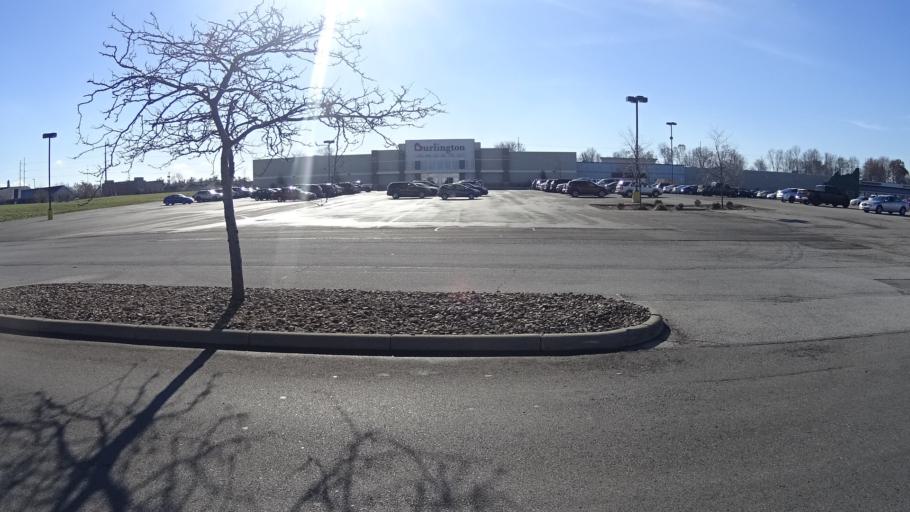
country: US
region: Ohio
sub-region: Lorain County
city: Sheffield
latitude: 41.4207
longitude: -82.0795
